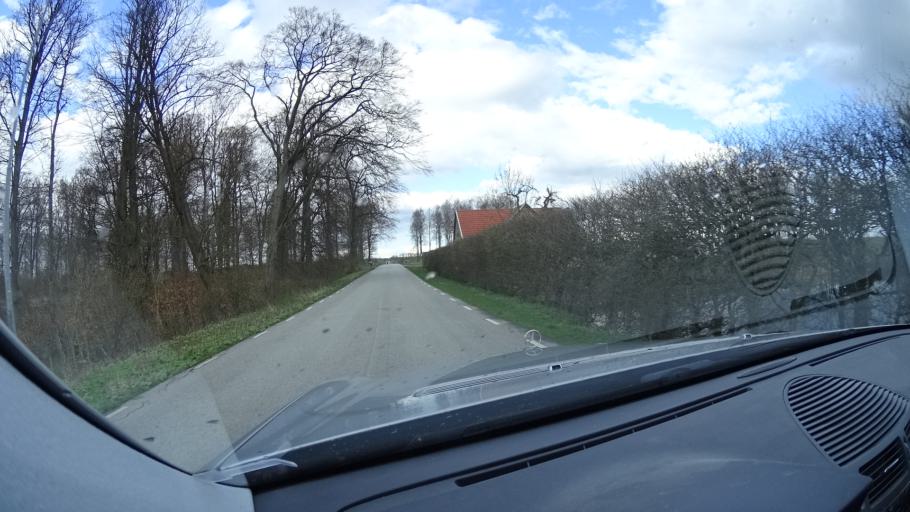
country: SE
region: Skane
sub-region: Eslovs Kommun
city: Eslov
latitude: 55.8064
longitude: 13.3739
